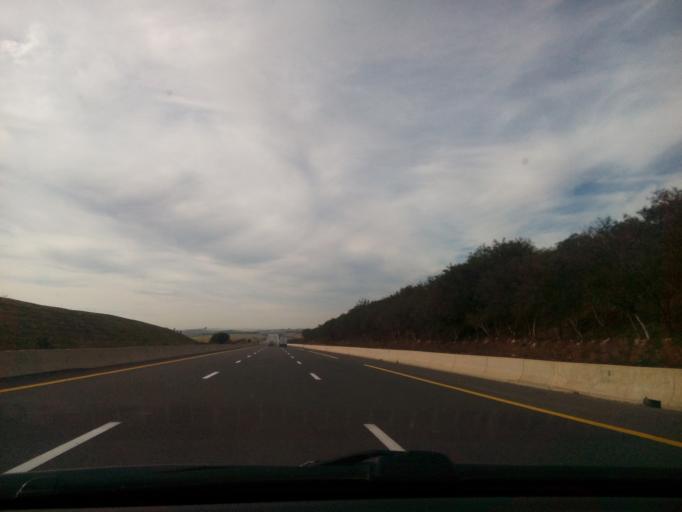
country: DZ
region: Sidi Bel Abbes
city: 'Ain el Berd
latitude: 35.3192
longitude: -0.5430
